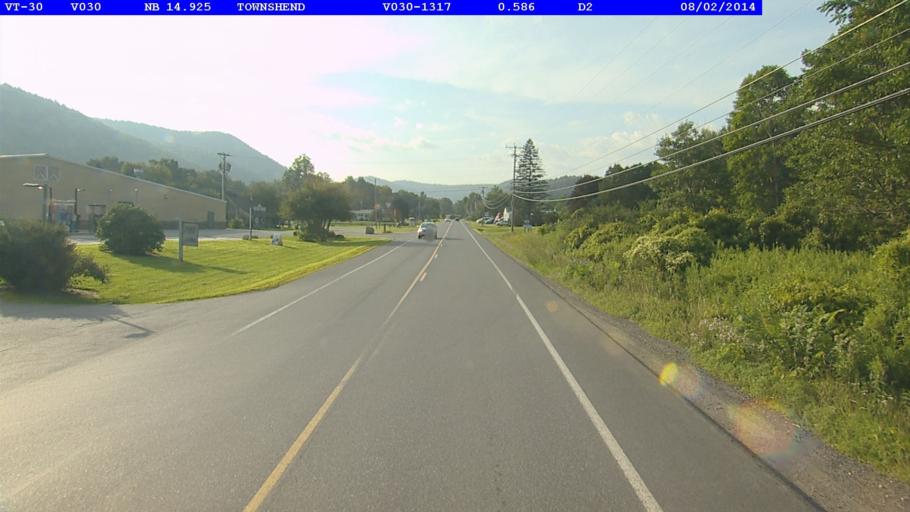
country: US
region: Vermont
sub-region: Windham County
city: Newfane
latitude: 43.0277
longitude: -72.6574
